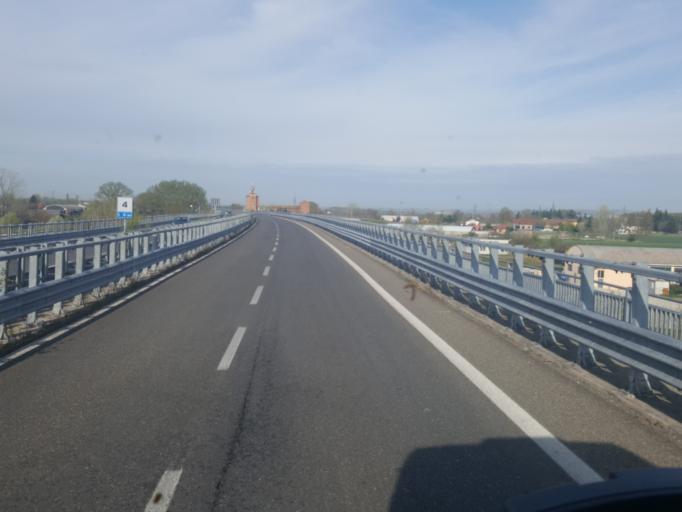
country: IT
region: Piedmont
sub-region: Provincia di Alessandria
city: Valle San Bartolomeo
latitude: 44.9349
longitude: 8.6201
